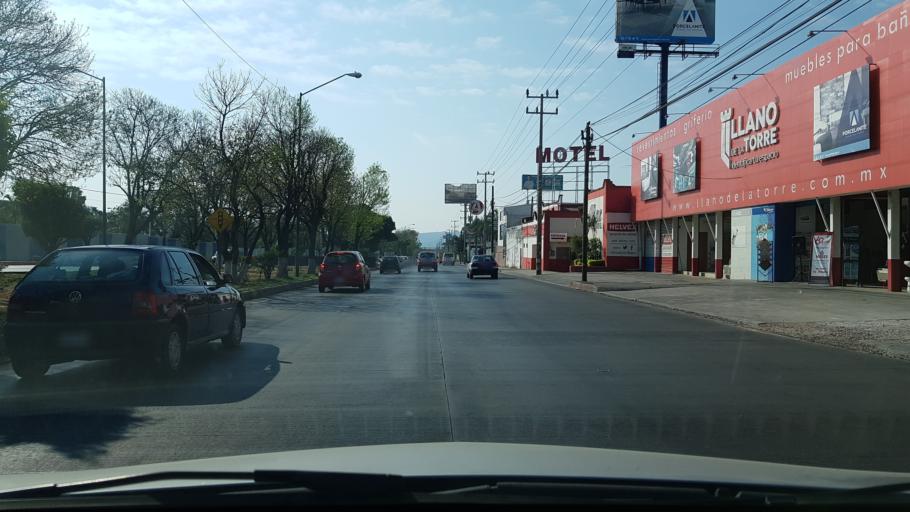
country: MX
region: Morelos
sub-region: Tepoztlan
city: Tetecolala
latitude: 18.9072
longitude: -99.1792
